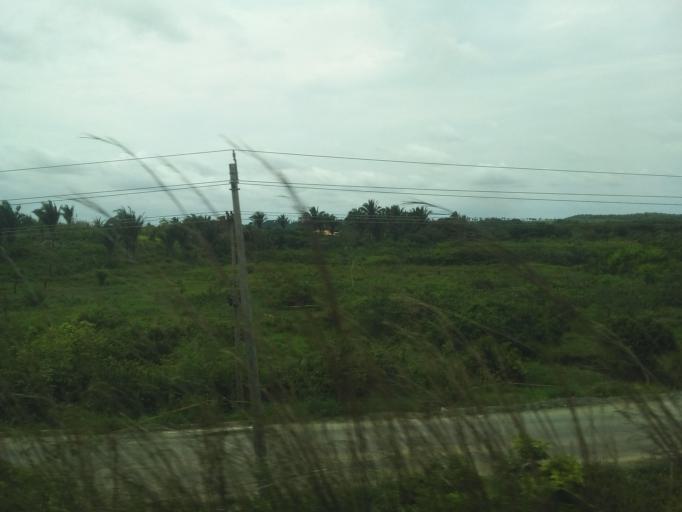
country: BR
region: Maranhao
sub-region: Santa Ines
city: Santa Ines
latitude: -3.6748
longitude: -45.8744
